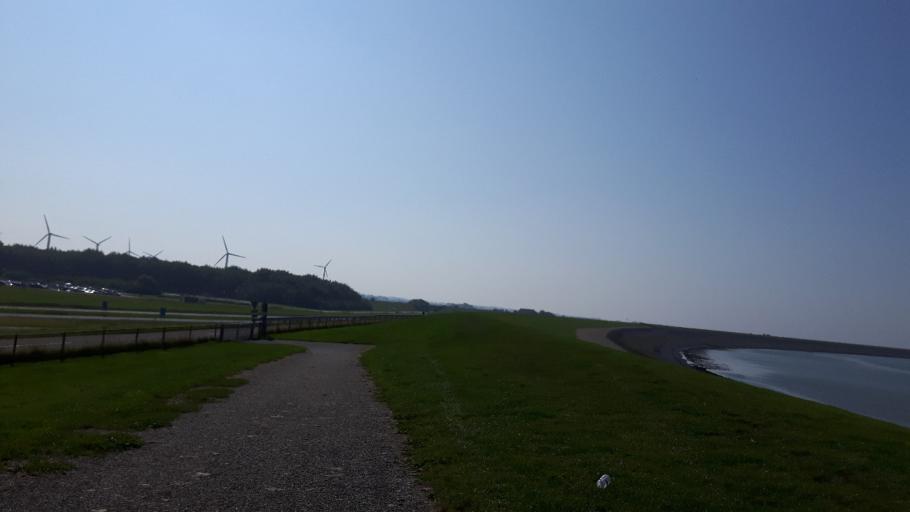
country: NL
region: Friesland
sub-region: Sudwest Fryslan
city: Makkum
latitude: 53.1016
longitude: 5.3820
